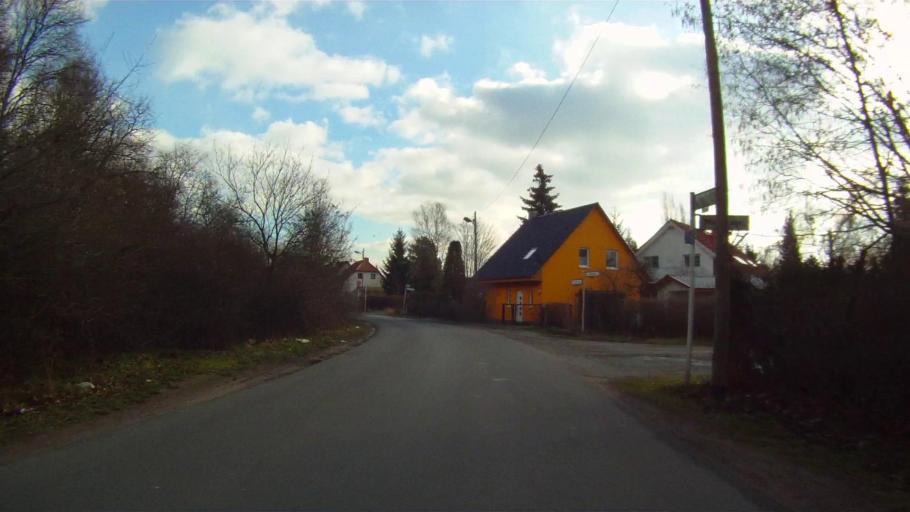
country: DE
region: Berlin
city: Kaulsdorf
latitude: 52.4897
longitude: 13.5798
